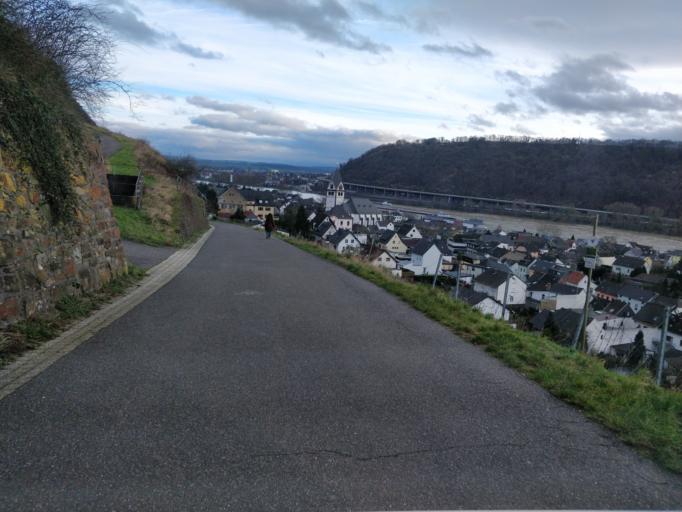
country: DE
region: Rheinland-Pfalz
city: Leutesdorf
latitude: 50.4553
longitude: 7.3841
